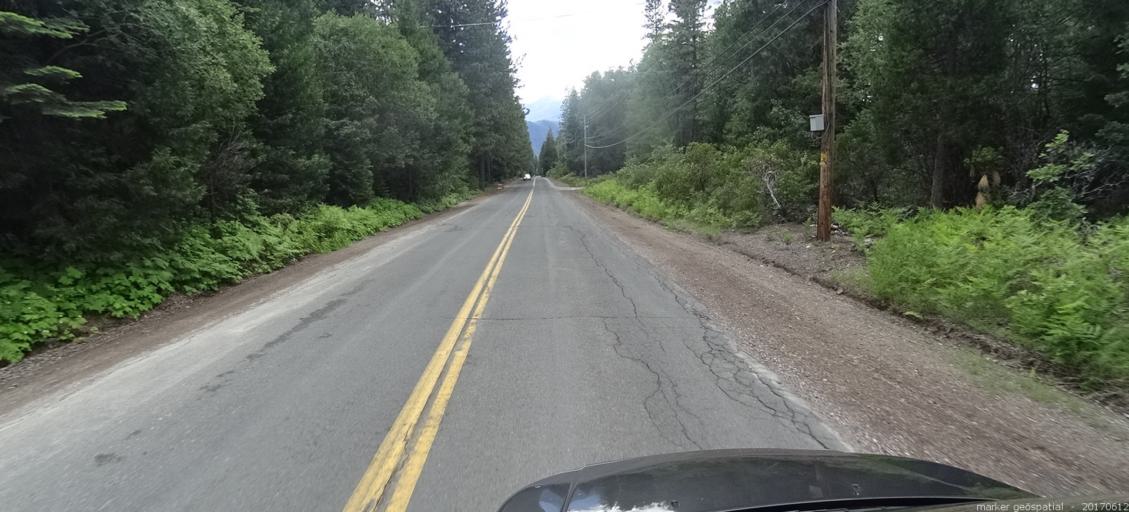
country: US
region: California
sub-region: Siskiyou County
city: Mount Shasta
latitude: 41.3122
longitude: -122.2945
